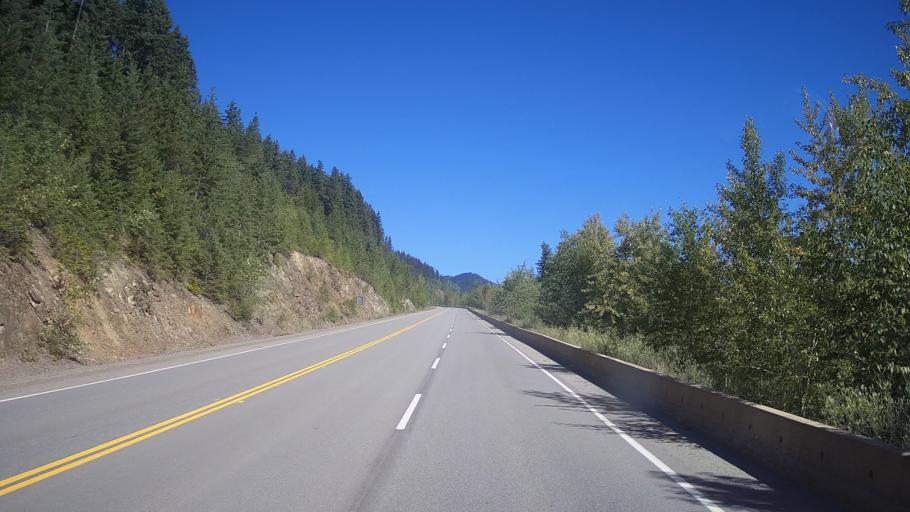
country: CA
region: British Columbia
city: Kamloops
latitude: 51.4780
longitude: -120.2584
